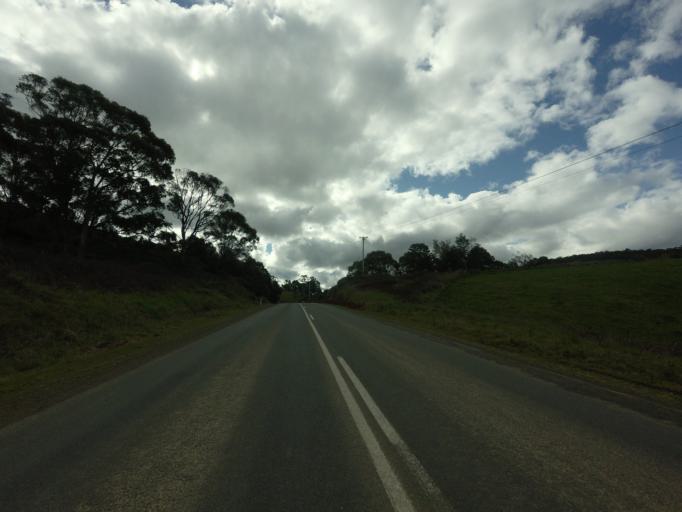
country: AU
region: Tasmania
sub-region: Huon Valley
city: Geeveston
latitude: -43.1834
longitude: 146.9538
